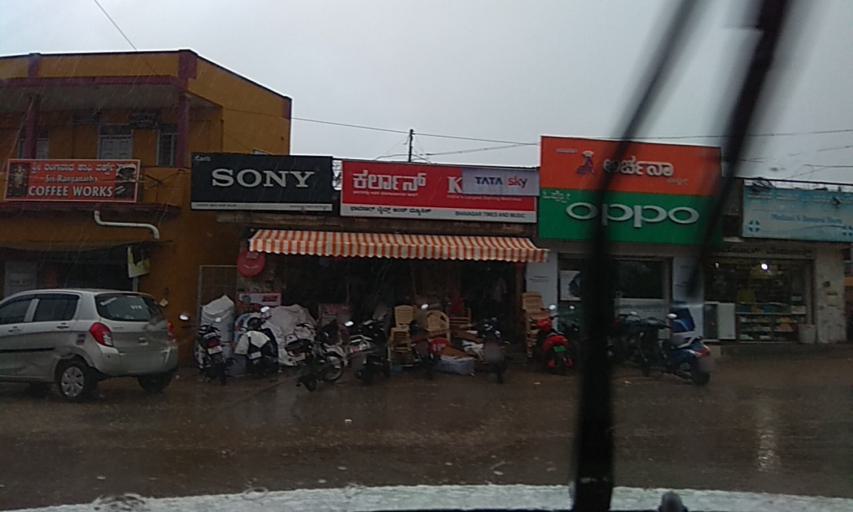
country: IN
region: Karnataka
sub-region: Chamrajnagar
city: Gundlupet
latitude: 11.8092
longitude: 76.6896
